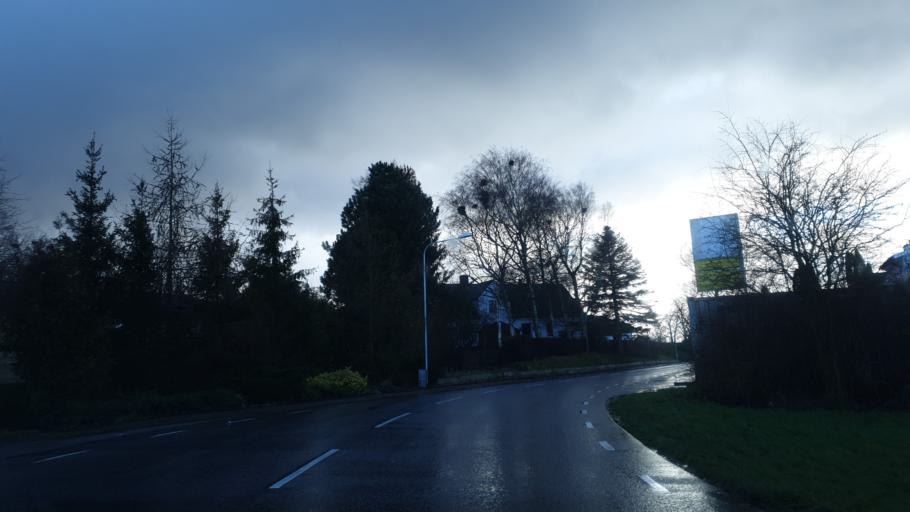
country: SE
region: Skane
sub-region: Skurups Kommun
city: Rydsgard
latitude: 55.4769
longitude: 13.5948
